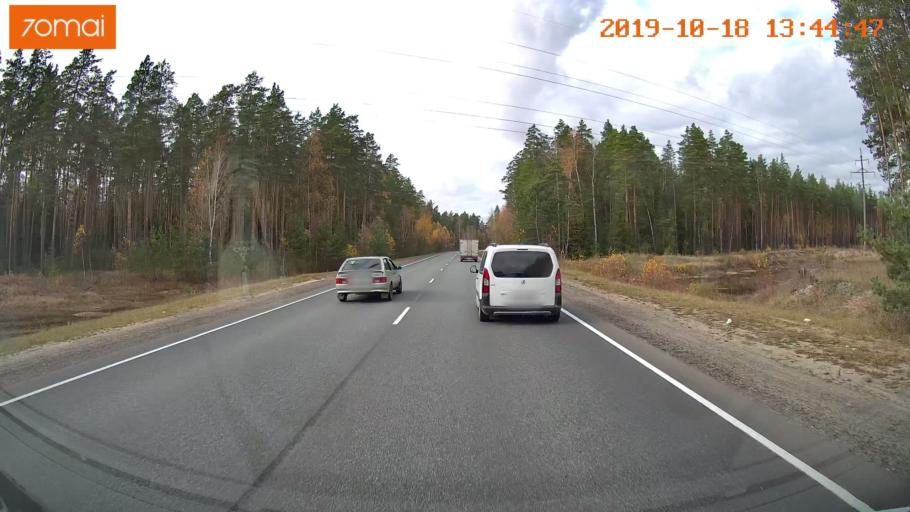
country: RU
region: Rjazan
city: Solotcha
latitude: 54.9396
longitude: 39.9559
